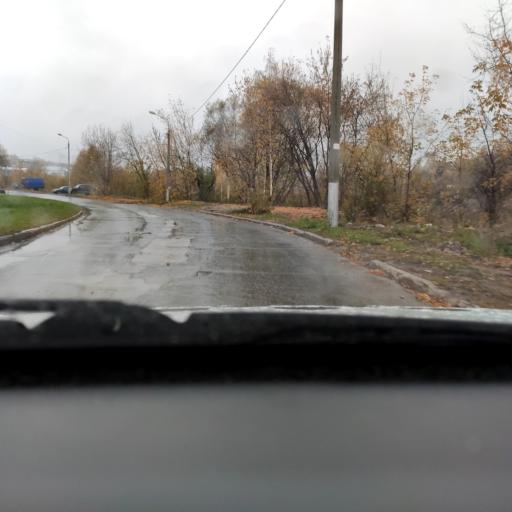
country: RU
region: Perm
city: Perm
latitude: 58.0122
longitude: 56.3115
